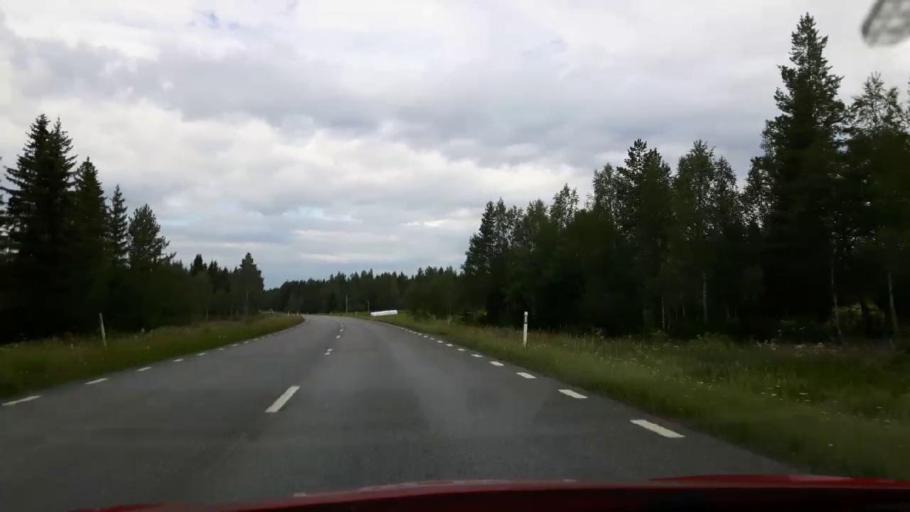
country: SE
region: Jaemtland
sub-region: Stroemsunds Kommun
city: Stroemsund
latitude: 63.5566
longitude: 15.3728
